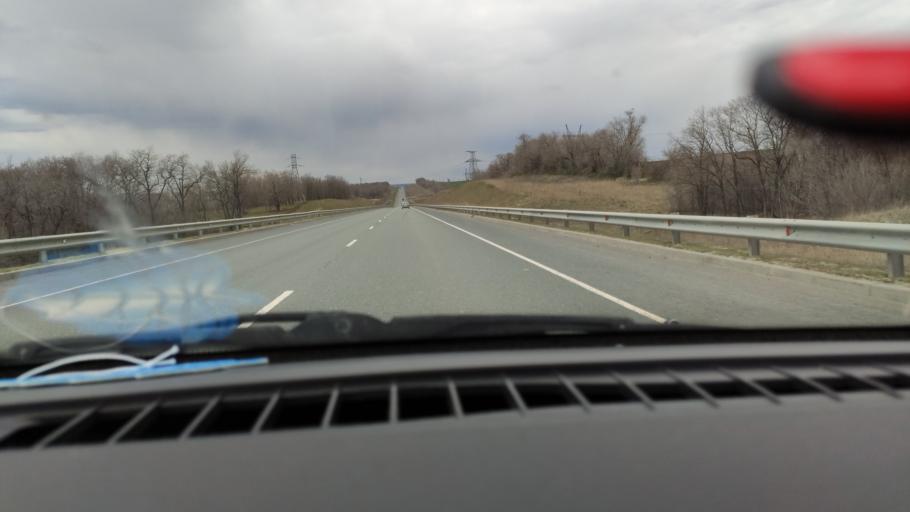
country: RU
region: Saratov
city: Yelshanka
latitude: 51.8230
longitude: 46.3215
